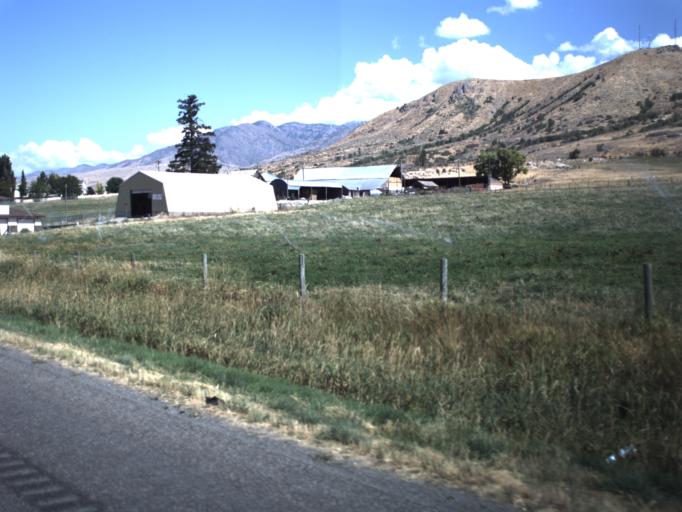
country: US
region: Utah
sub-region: Cache County
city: Smithfield
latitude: 41.8662
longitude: -111.8289
